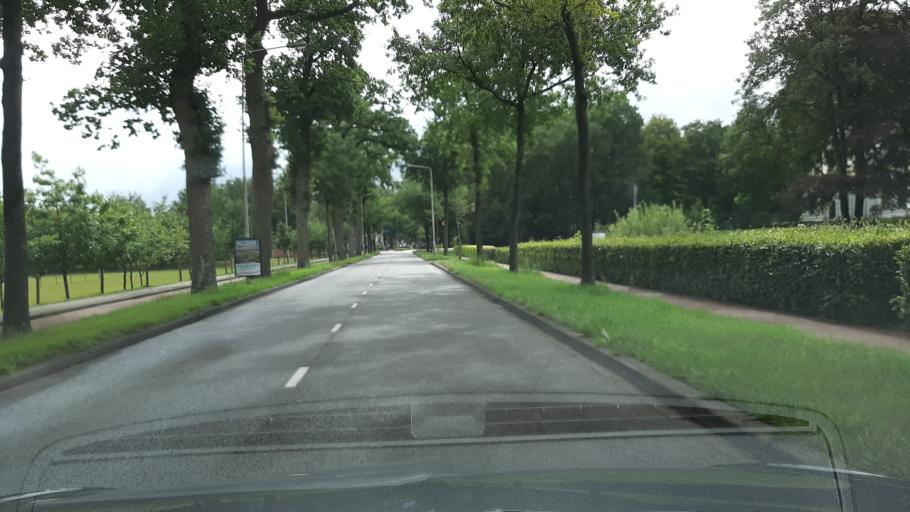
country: NL
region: Friesland
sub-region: Gemeente Heerenveen
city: Oranjewoud
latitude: 52.9399
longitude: 5.9481
